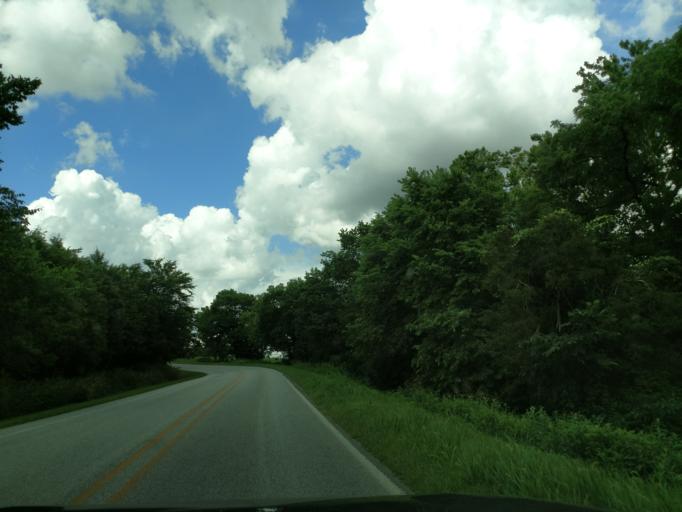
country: US
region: Arkansas
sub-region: Carroll County
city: Berryville
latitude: 36.4188
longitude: -93.5581
